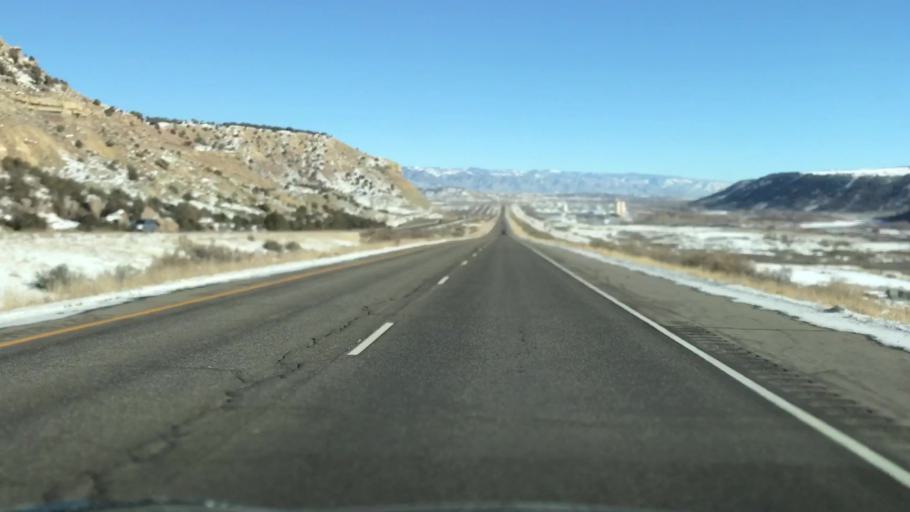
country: US
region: Colorado
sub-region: Garfield County
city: Rifle
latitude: 39.5090
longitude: -107.8776
